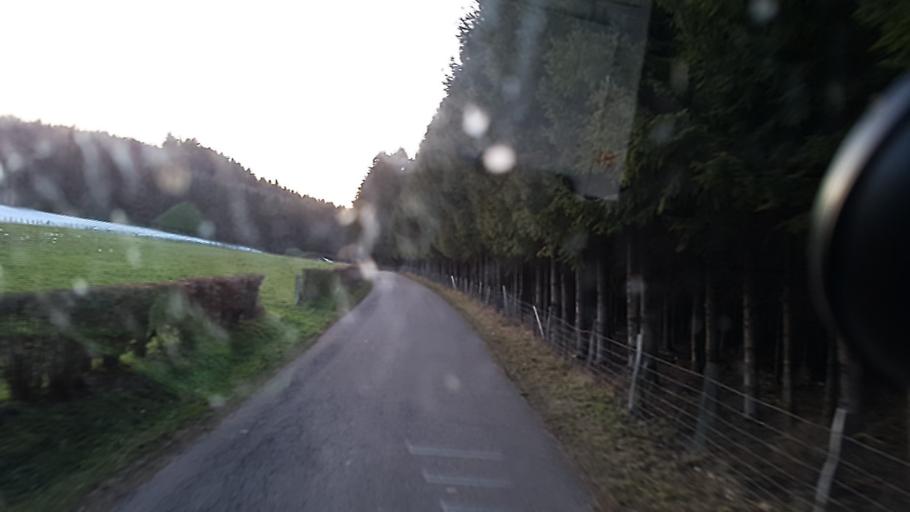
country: BE
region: Wallonia
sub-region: Province du Luxembourg
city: Daverdisse
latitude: 50.0087
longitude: 5.1410
